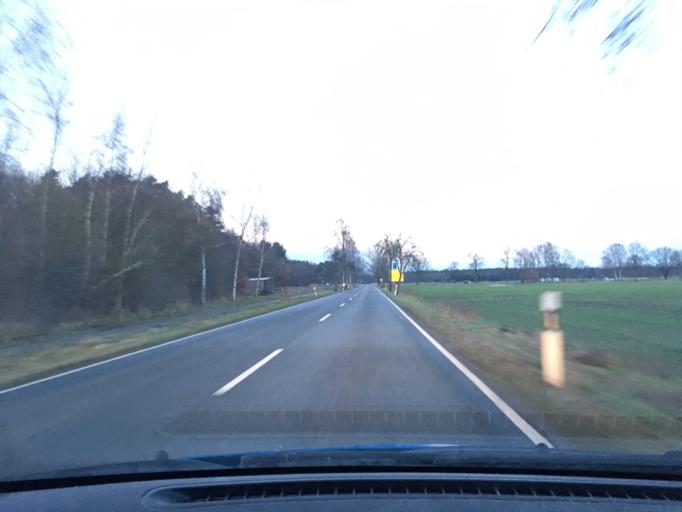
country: DE
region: Lower Saxony
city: Isernhagen Farster Bauerschaft
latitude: 52.5139
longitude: 9.8597
